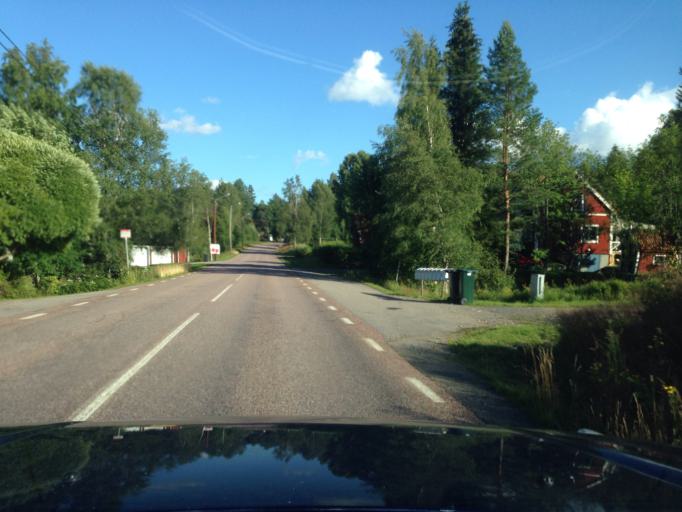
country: SE
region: Dalarna
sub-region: Ludvika Kommun
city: Grangesberg
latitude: 60.1393
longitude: 14.9994
